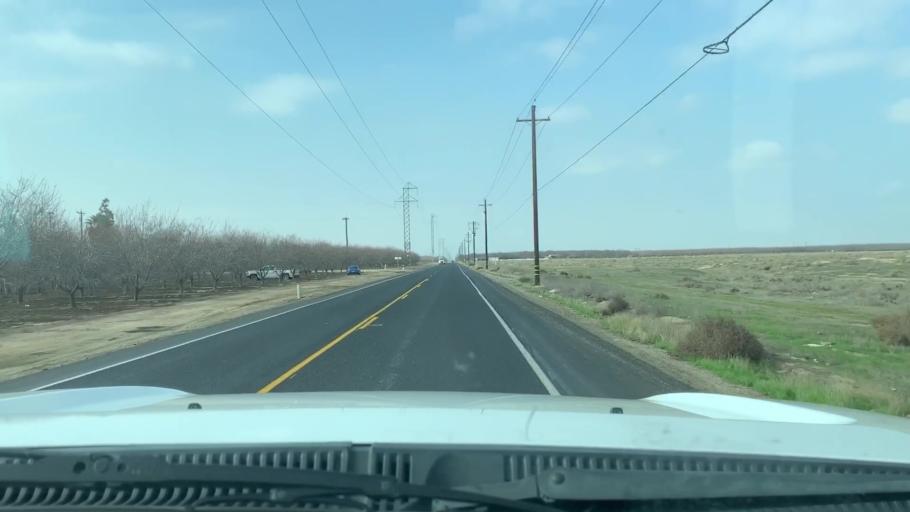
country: US
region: California
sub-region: Kern County
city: Shafter
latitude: 35.4418
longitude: -119.2878
